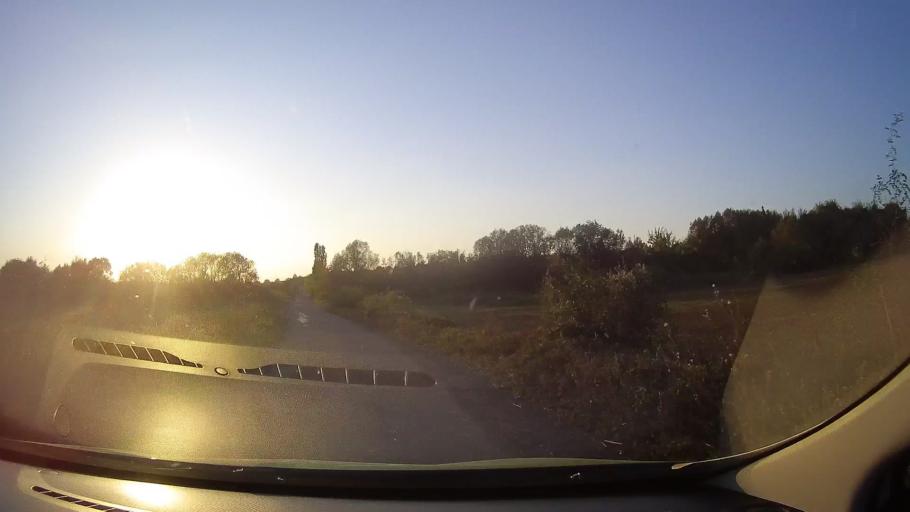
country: RO
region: Bihor
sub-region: Comuna Salard
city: Salard
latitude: 47.2499
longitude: 22.0139
